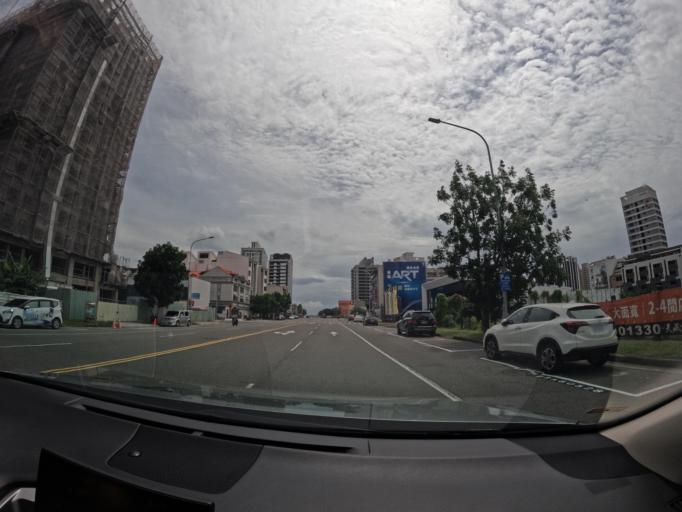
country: TW
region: Kaohsiung
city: Kaohsiung
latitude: 22.7267
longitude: 120.2793
